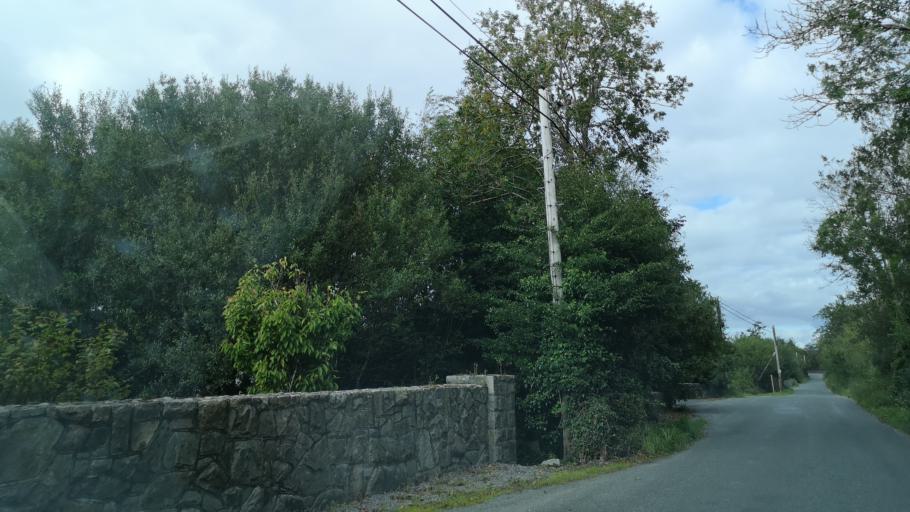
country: IE
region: Connaught
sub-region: County Galway
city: Moycullen
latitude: 53.3188
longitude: -9.1484
